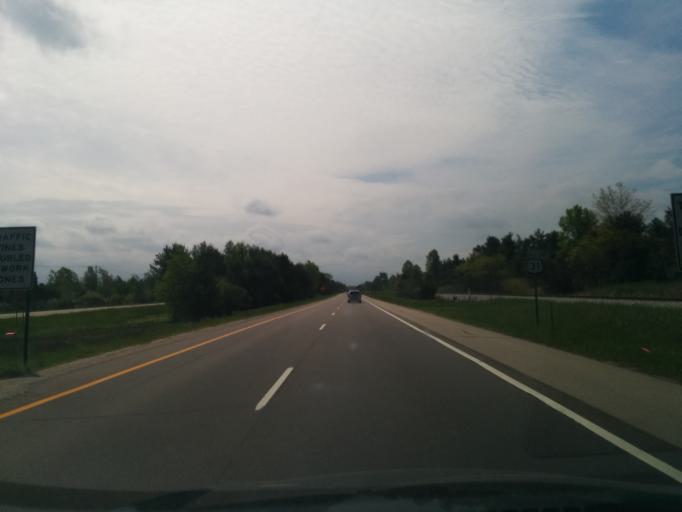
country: US
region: Michigan
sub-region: Ottawa County
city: Grand Haven
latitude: 42.9412
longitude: -86.1607
